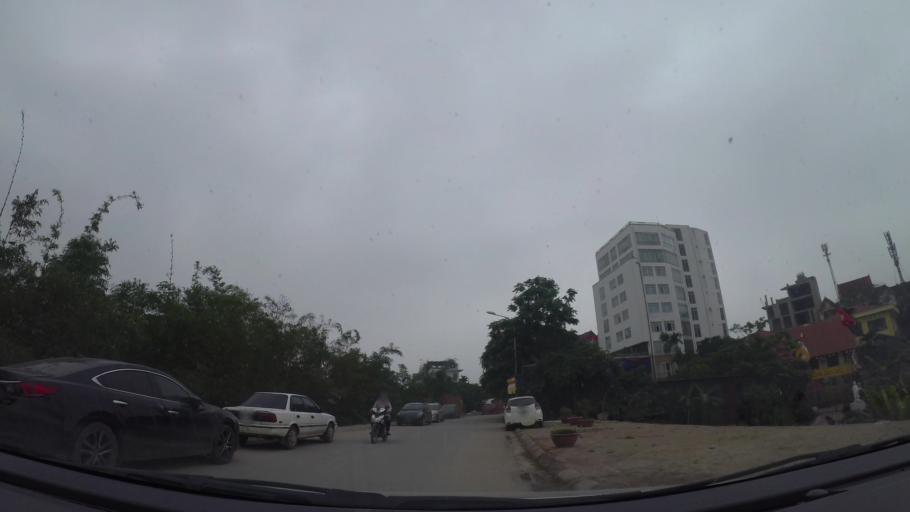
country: VN
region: Ha Noi
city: Tay Ho
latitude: 21.0737
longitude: 105.8213
